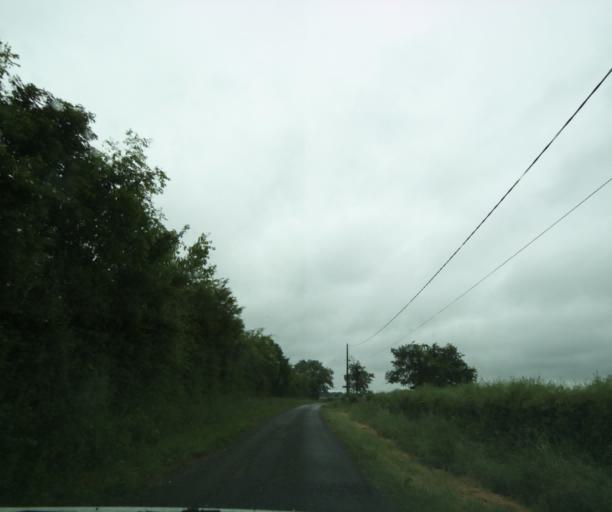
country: FR
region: Bourgogne
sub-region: Departement de Saone-et-Loire
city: Palinges
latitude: 46.5543
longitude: 4.1983
